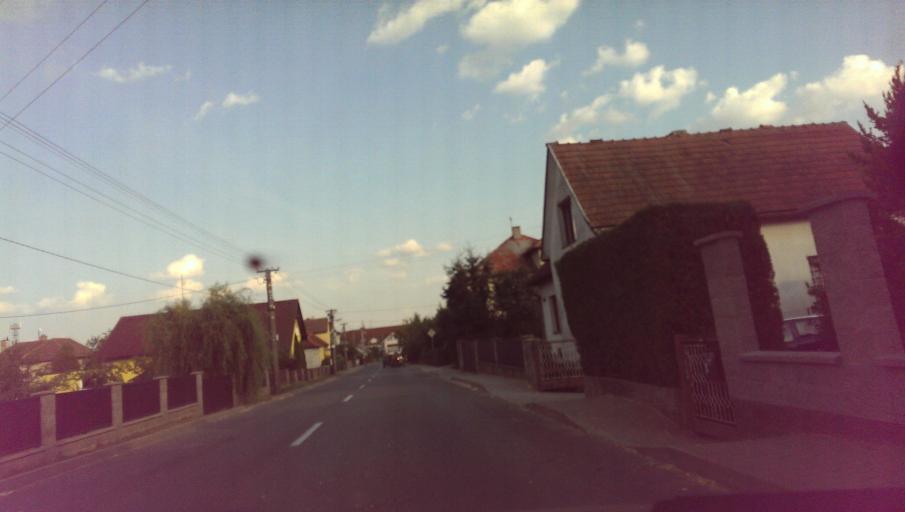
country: CZ
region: Zlin
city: Hvozdna
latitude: 49.2581
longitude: 17.7540
